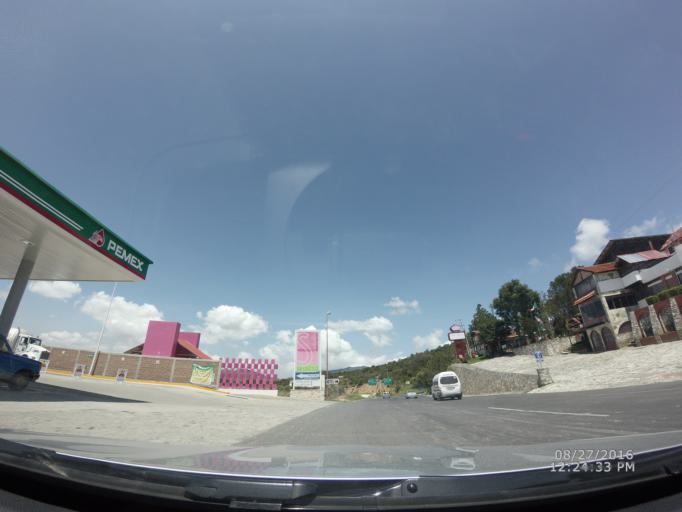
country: MX
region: Hidalgo
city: Mineral del Monte
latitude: 20.1403
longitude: -98.6908
